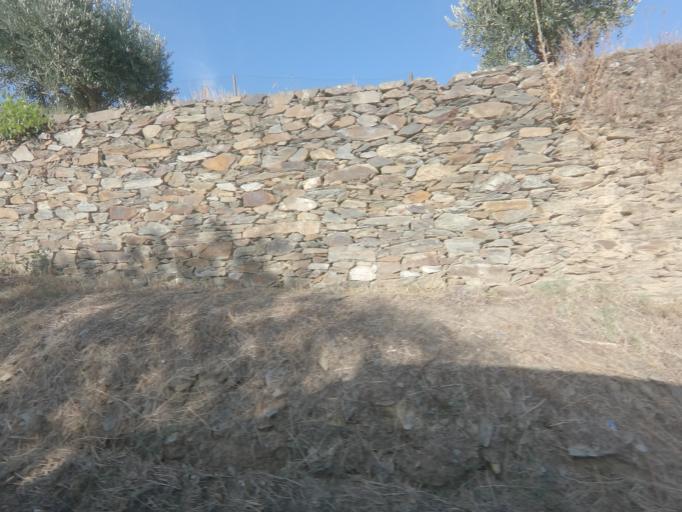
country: PT
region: Vila Real
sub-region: Sabrosa
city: Vilela
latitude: 41.2073
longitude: -7.5416
